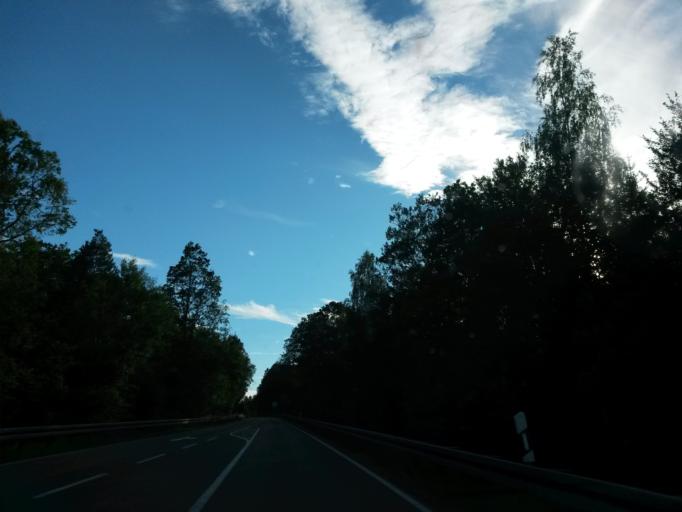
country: DE
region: Baden-Wuerttemberg
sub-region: Regierungsbezirk Stuttgart
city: Wort
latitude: 49.0363
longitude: 10.2415
